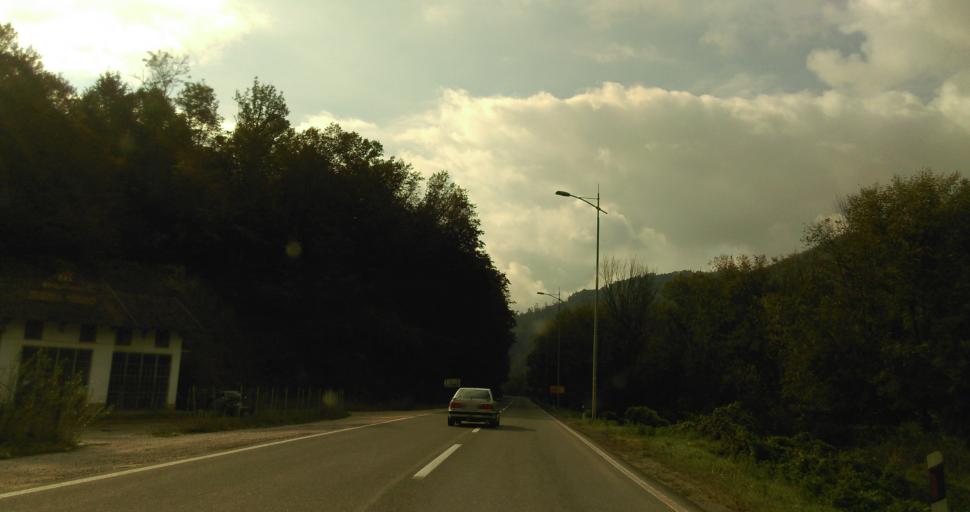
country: RS
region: Central Serbia
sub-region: Kolubarski Okrug
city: Ljig
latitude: 44.2113
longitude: 20.2260
